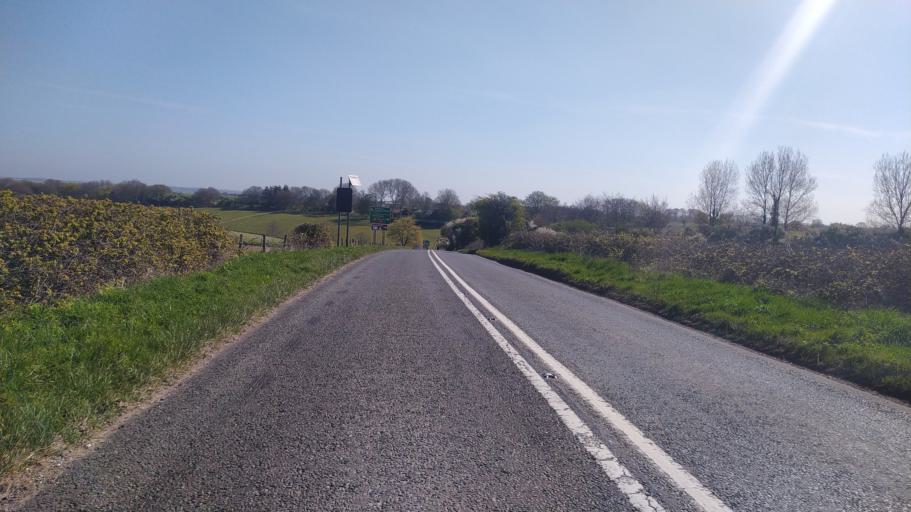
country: GB
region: England
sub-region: Wiltshire
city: Bishopstone
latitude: 51.0148
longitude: -1.8585
